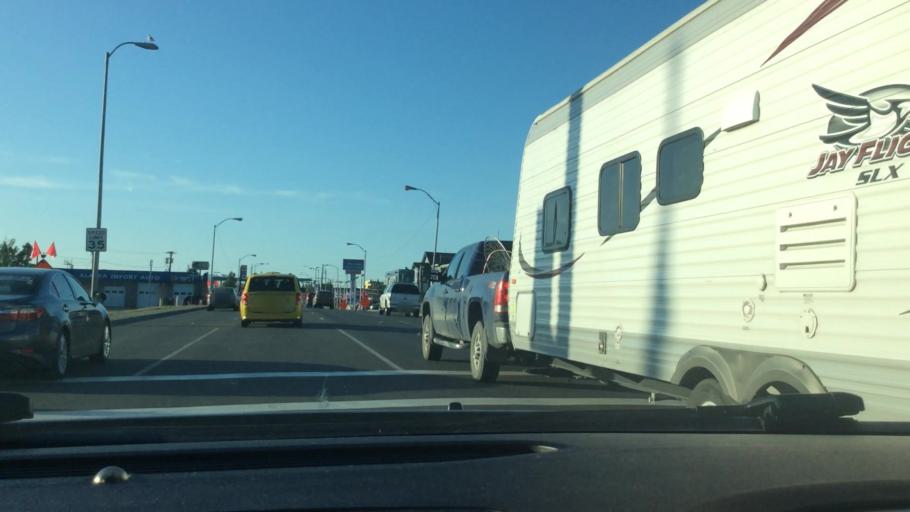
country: US
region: Alaska
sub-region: Anchorage Municipality
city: Anchorage
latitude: 61.2140
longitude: -149.8658
